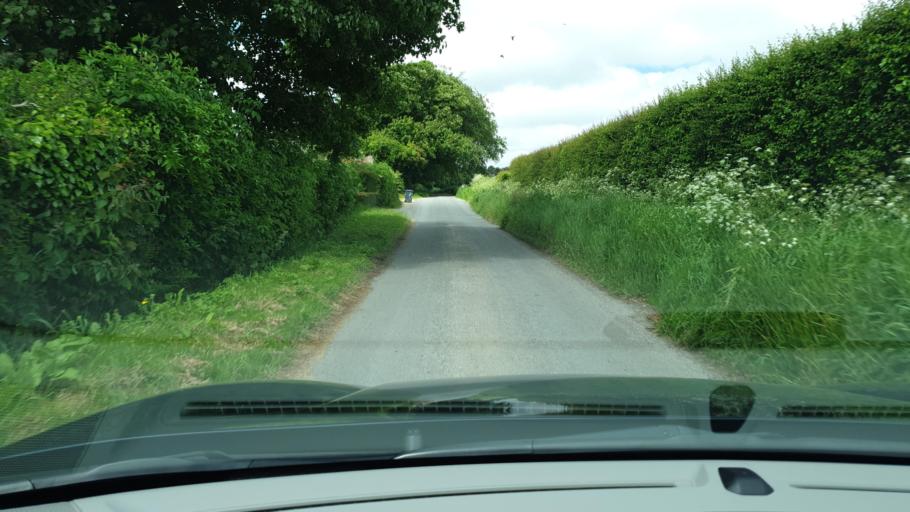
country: IE
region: Leinster
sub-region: An Mhi
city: Slane
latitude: 53.7350
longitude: -6.5565
